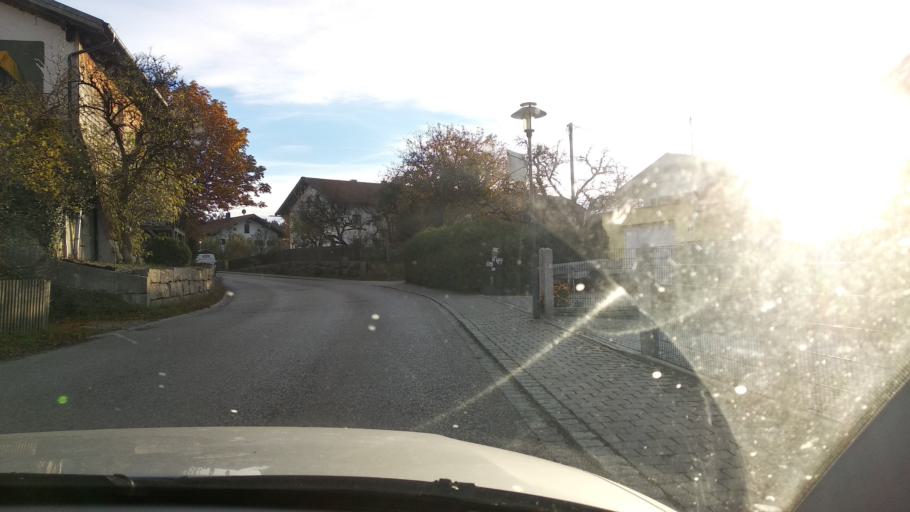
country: DE
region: Bavaria
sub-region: Upper Bavaria
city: Zorneding
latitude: 48.0603
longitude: 11.8507
